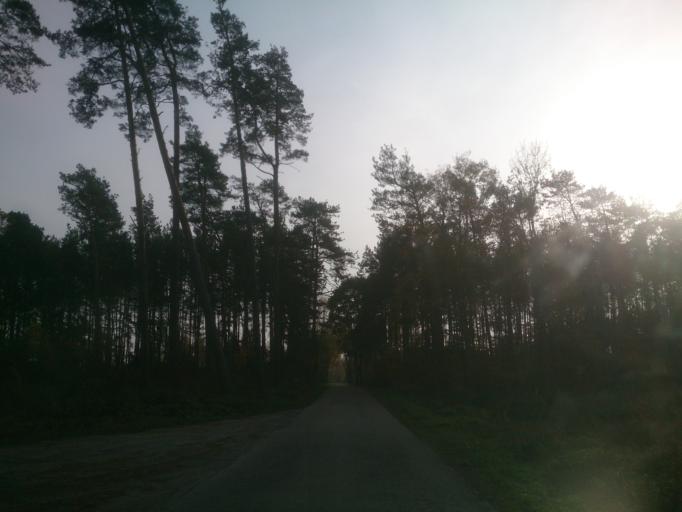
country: PL
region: Kujawsko-Pomorskie
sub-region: Powiat brodnicki
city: Brodnica
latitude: 53.3431
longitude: 19.3531
